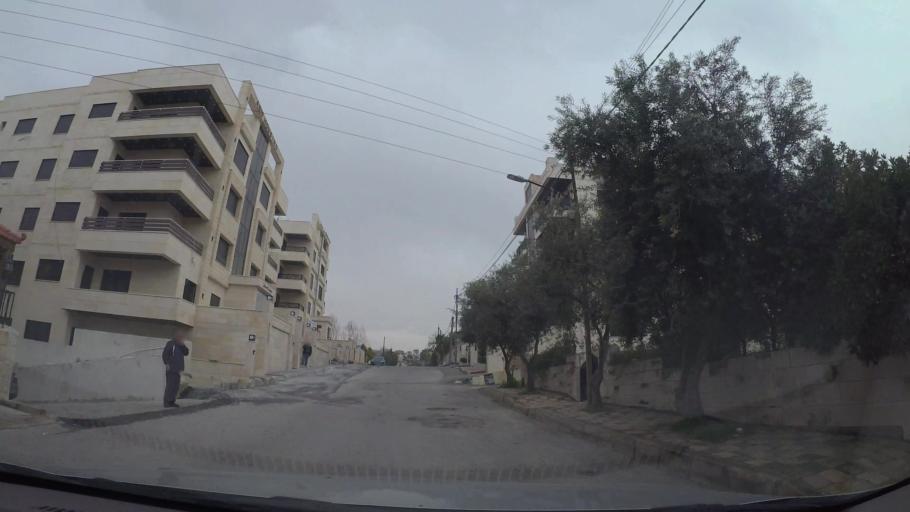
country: JO
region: Amman
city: Umm as Summaq
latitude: 31.8905
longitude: 35.8534
